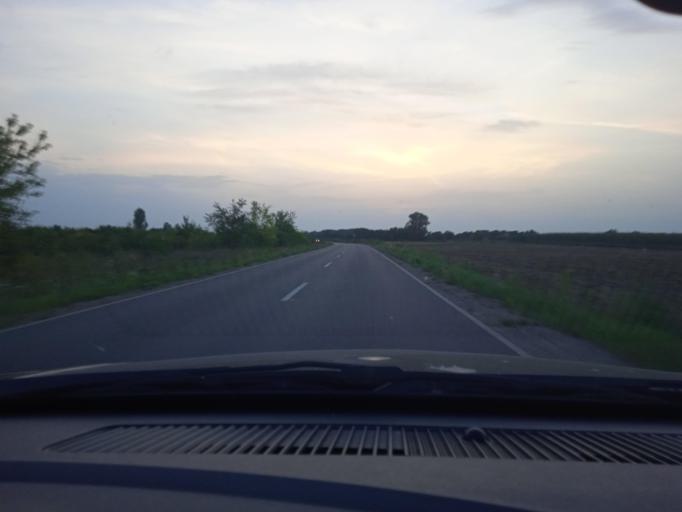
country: PL
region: Masovian Voivodeship
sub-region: Powiat nowodworski
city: Pomiechowek
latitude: 52.4640
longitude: 20.7115
